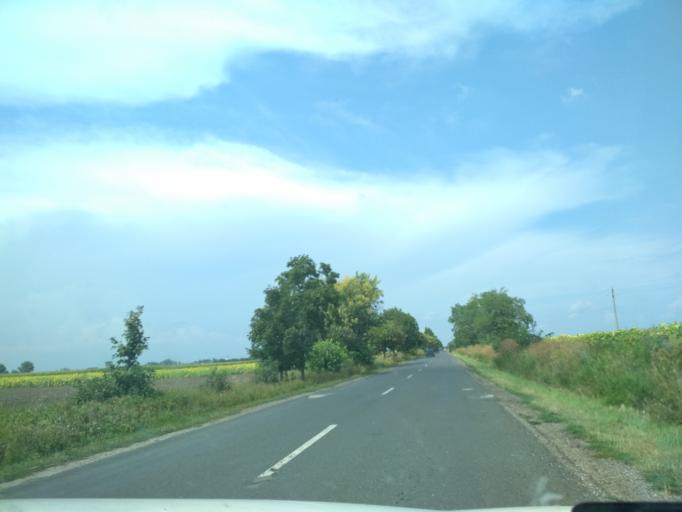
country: HU
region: Jasz-Nagykun-Szolnok
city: Tiszaszolos
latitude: 47.5386
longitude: 20.7167
